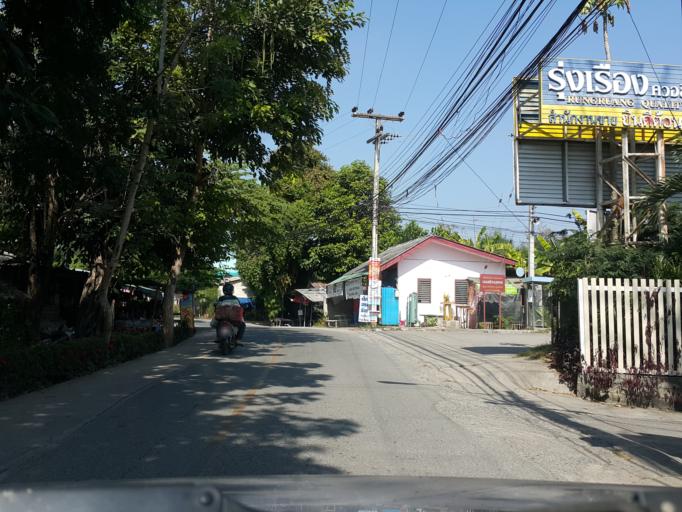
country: TH
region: Chiang Mai
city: San Sai
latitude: 18.8346
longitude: 99.0202
